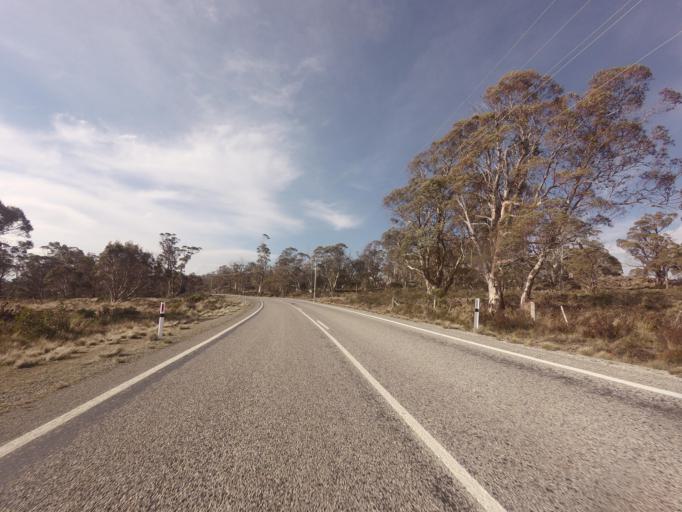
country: AU
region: Tasmania
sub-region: Meander Valley
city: Deloraine
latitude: -41.9924
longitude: 146.7070
